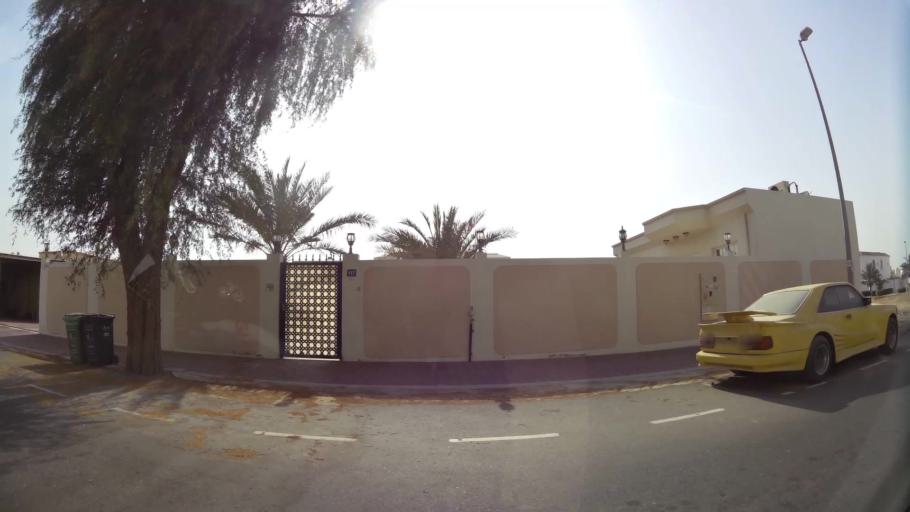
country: AE
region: Ash Shariqah
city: Sharjah
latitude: 25.2544
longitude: 55.4522
